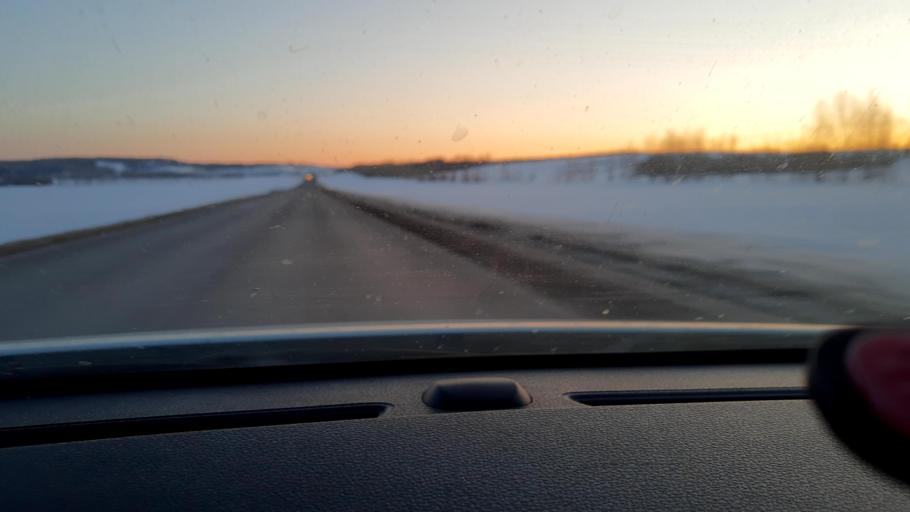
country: RU
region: Bashkortostan
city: Avdon
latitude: 54.4418
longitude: 55.8385
